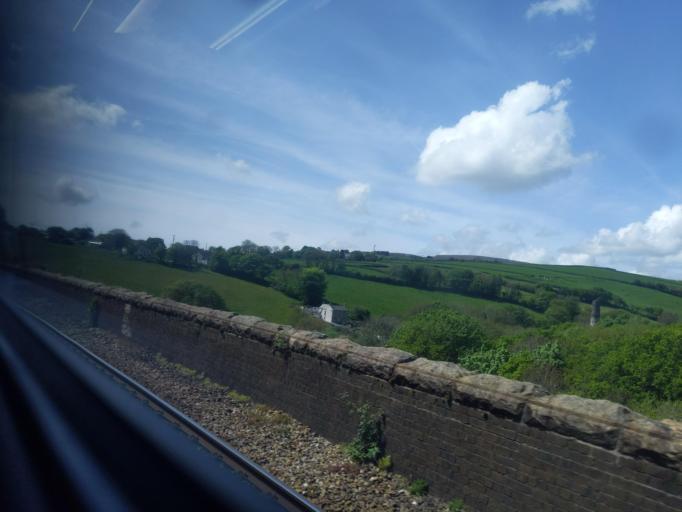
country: GB
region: England
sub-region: Cornwall
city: St Austell
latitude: 50.3430
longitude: -4.8130
